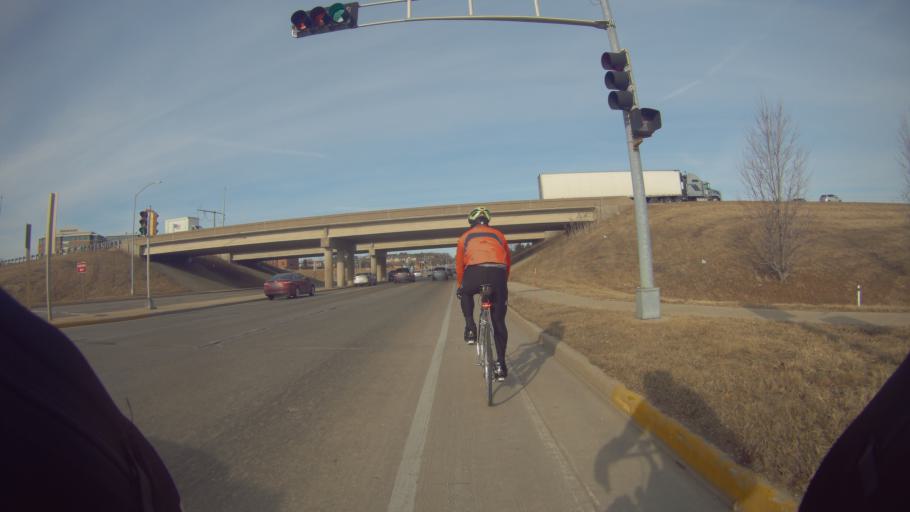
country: US
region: Wisconsin
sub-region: Dane County
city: Middleton
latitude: 43.0750
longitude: -89.5215
